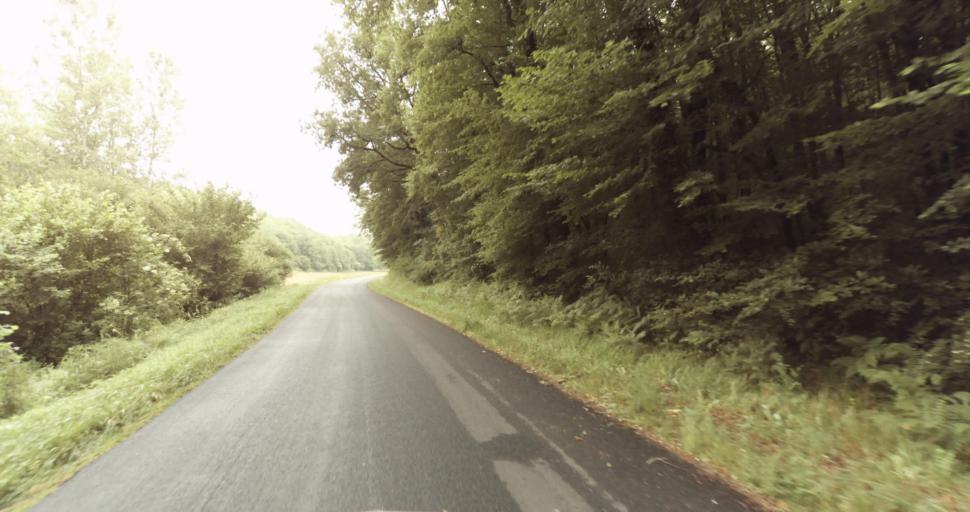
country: FR
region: Aquitaine
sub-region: Departement de la Dordogne
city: Lalinde
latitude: 44.8668
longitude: 0.7733
